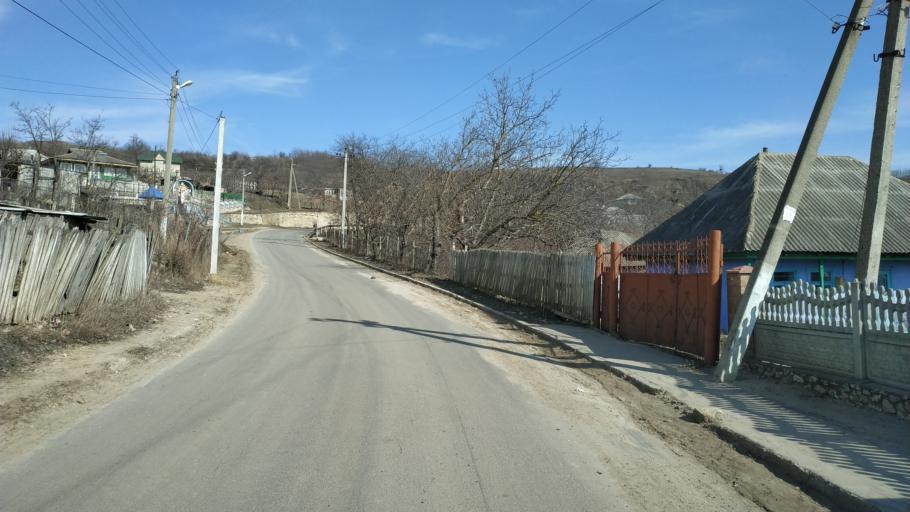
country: MD
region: Nisporeni
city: Nisporeni
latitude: 47.2248
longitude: 28.0432
